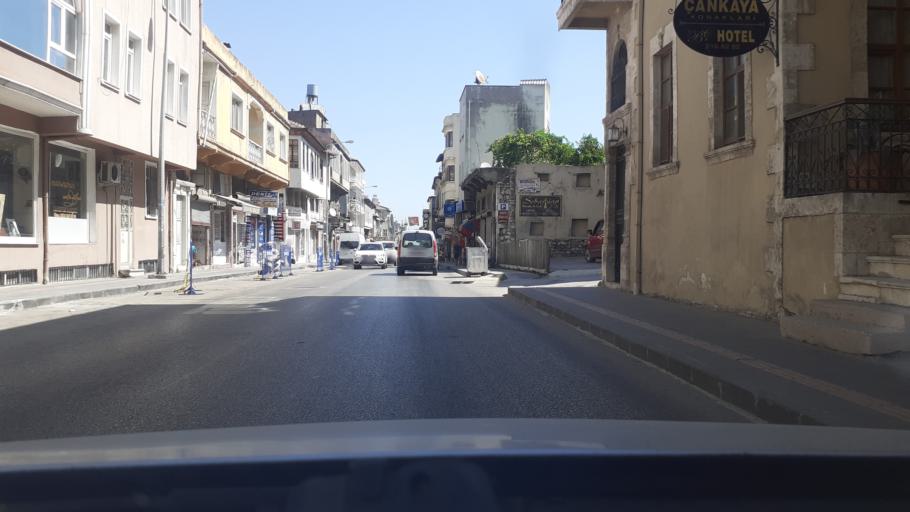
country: TR
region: Hatay
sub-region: Antakya Ilcesi
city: Antakya
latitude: 36.1978
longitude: 36.1620
